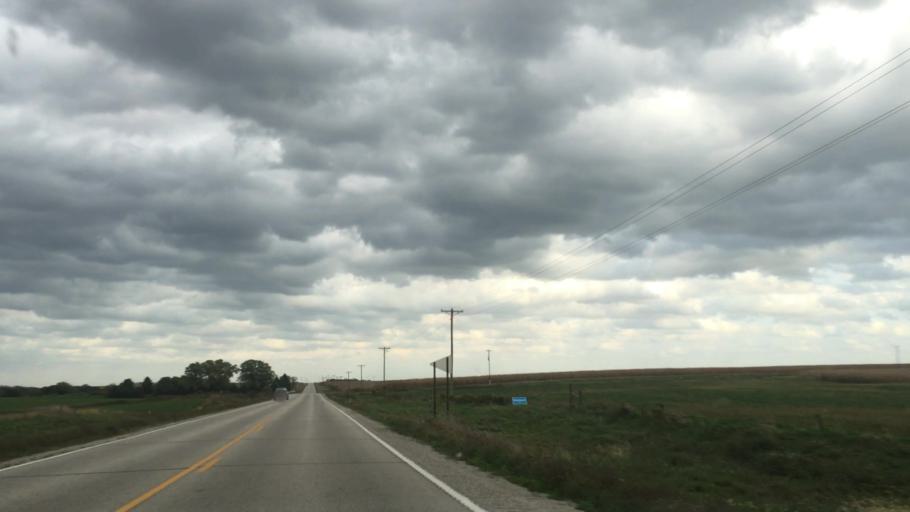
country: US
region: Minnesota
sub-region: Fillmore County
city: Preston
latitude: 43.7318
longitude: -92.0768
